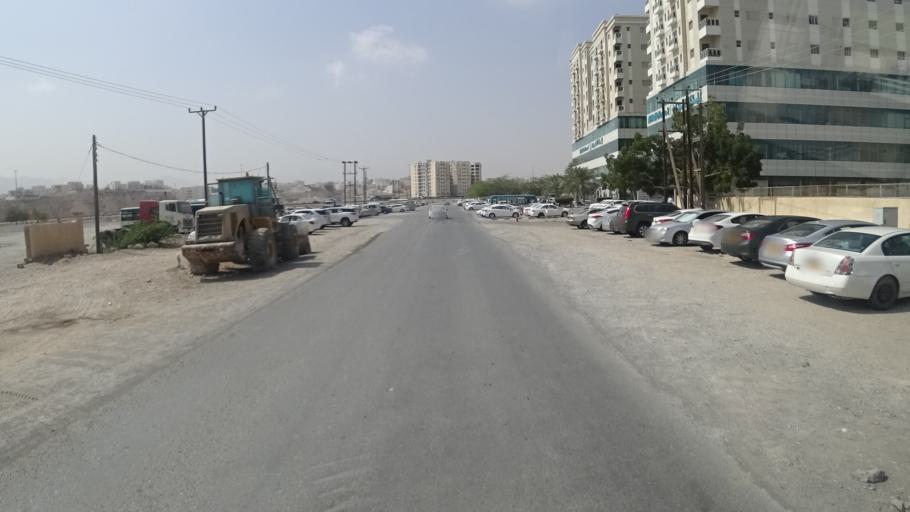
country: OM
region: Muhafazat Masqat
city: Bawshar
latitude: 23.5660
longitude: 58.3473
